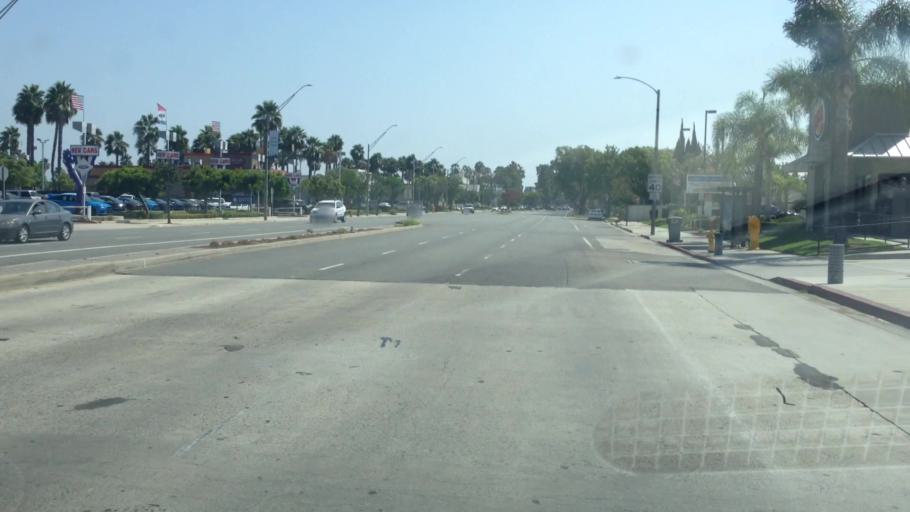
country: US
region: California
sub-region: Los Angeles County
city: Signal Hill
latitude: 33.8103
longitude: -118.1254
